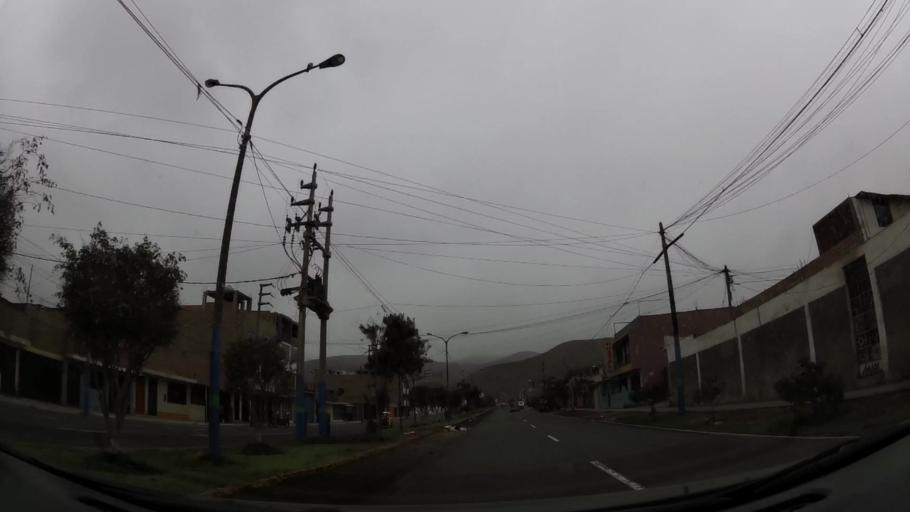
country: PE
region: Lima
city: Ventanilla
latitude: -11.8822
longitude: -77.1294
